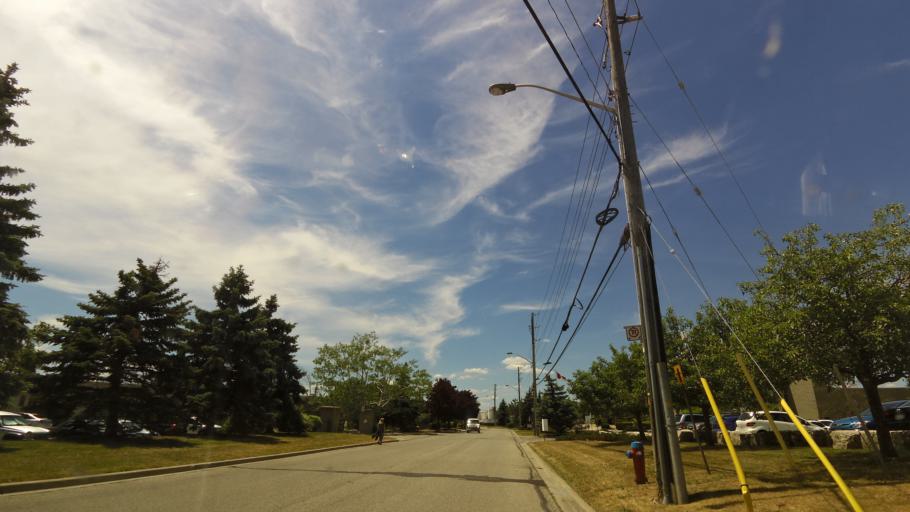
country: CA
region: Ontario
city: Burlington
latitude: 43.3972
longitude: -79.7635
